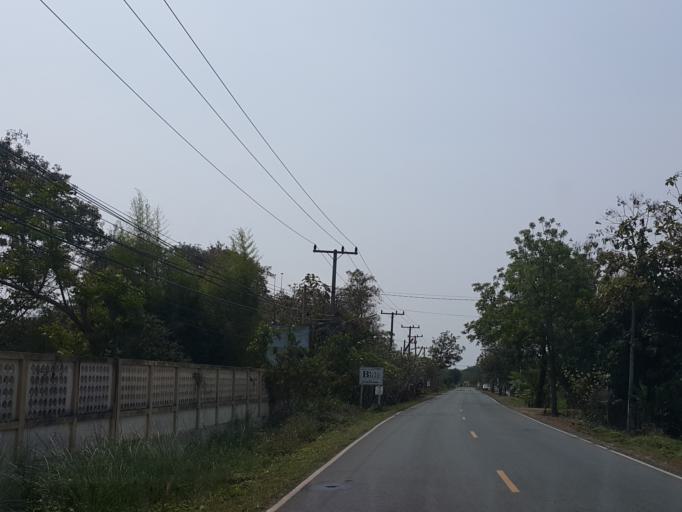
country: TH
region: Chiang Mai
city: San Kamphaeng
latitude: 18.6935
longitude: 99.1031
